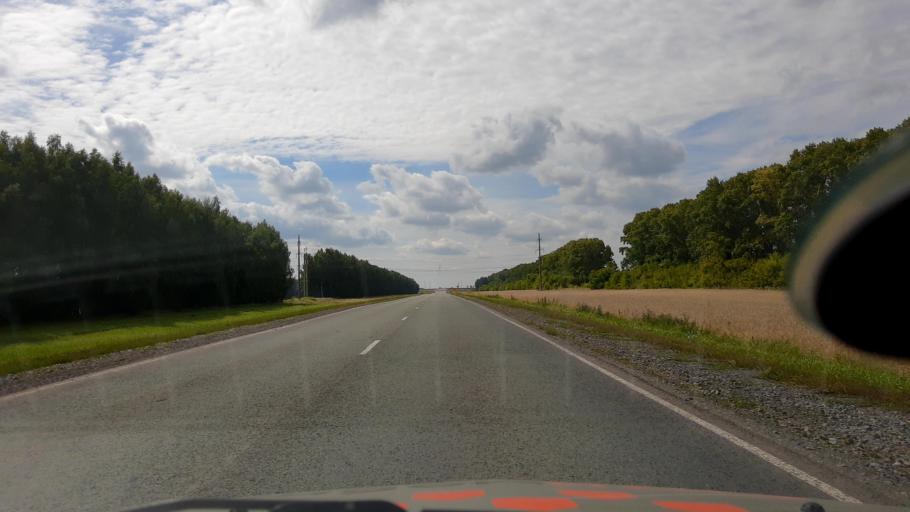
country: RU
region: Bashkortostan
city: Buzdyak
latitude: 54.6594
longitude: 54.5415
